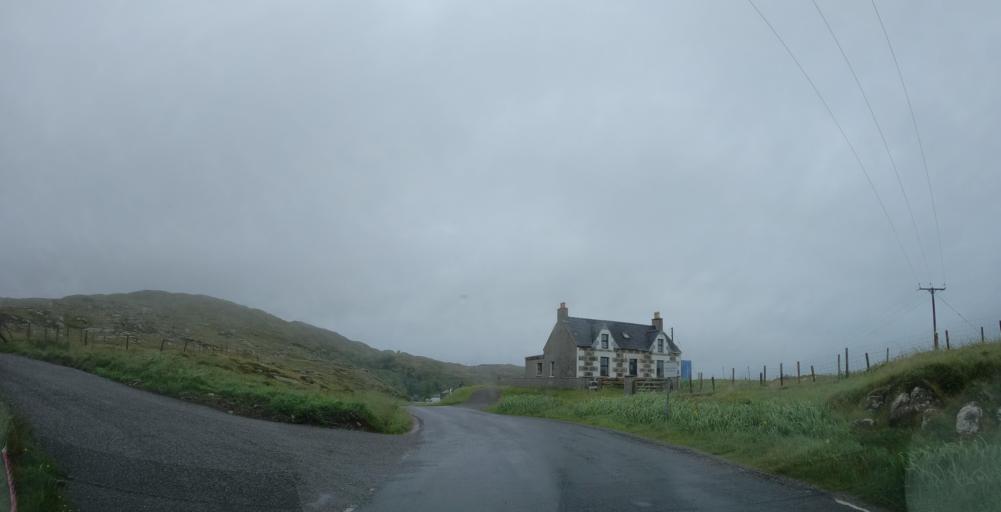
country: GB
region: Scotland
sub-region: Eilean Siar
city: Barra
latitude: 57.0097
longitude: -7.4297
